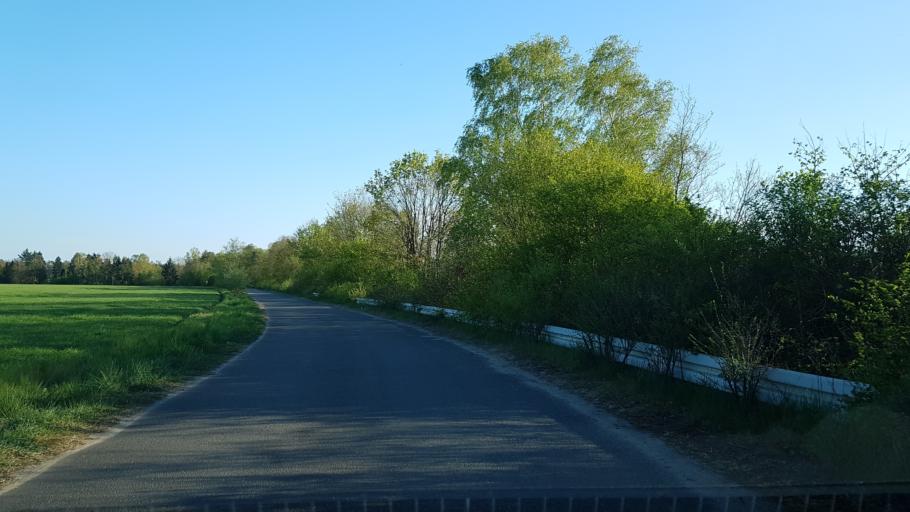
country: DE
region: Lower Saxony
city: Wendisch Evern
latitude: 53.2211
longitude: 10.4933
